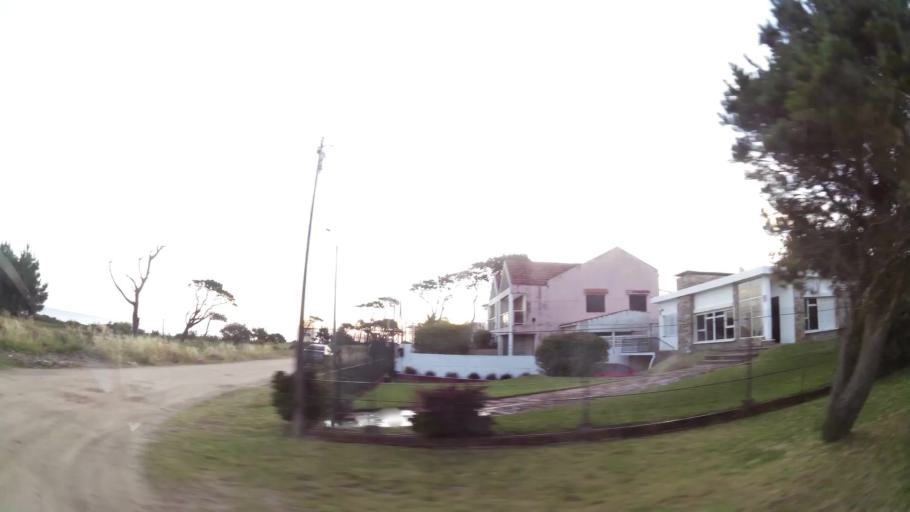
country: UY
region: Canelones
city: Atlantida
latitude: -34.7763
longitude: -55.7440
